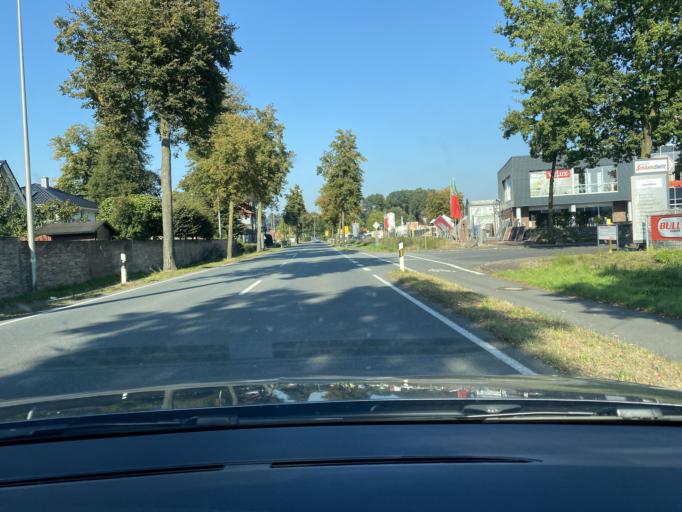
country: DE
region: North Rhine-Westphalia
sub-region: Regierungsbezirk Munster
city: Gronau
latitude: 52.1891
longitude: 7.0300
